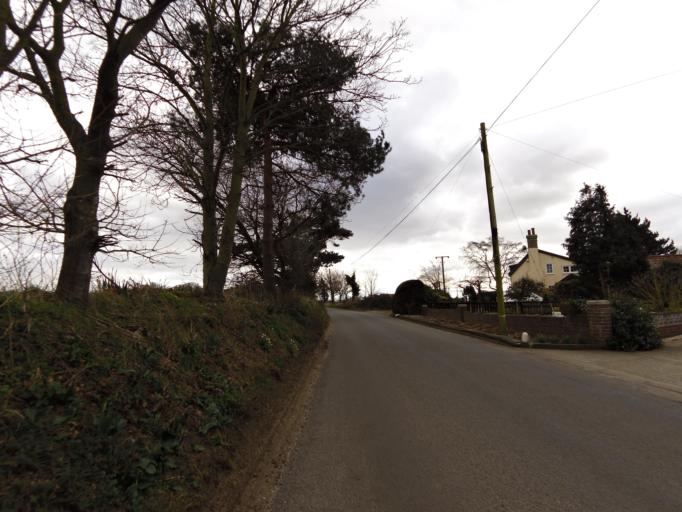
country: GB
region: England
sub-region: Suffolk
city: Shotley Gate
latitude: 52.0218
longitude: 1.2995
